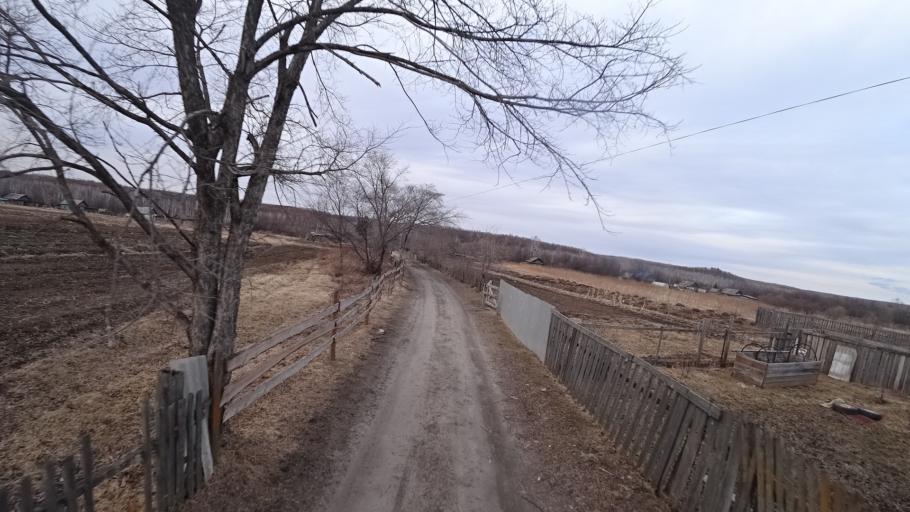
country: RU
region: Amur
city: Bureya
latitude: 50.0203
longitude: 129.7704
